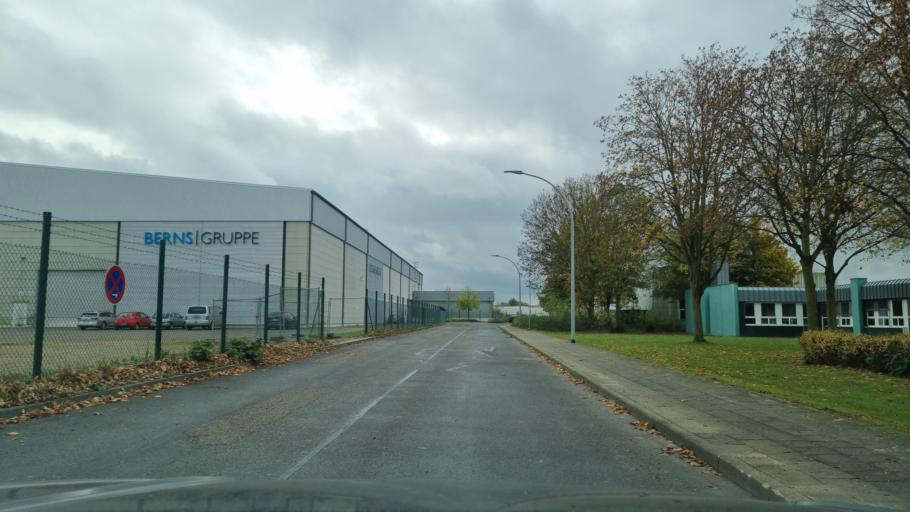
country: DE
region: North Rhine-Westphalia
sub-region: Regierungsbezirk Dusseldorf
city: Kleve
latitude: 51.8076
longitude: 6.1430
